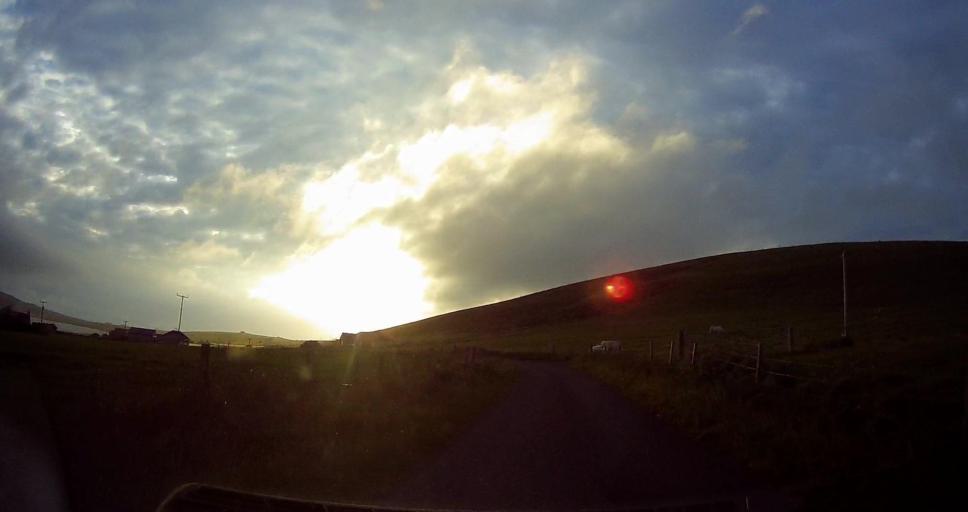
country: GB
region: Scotland
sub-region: Orkney Islands
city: Stromness
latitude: 59.1154
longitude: -3.2552
